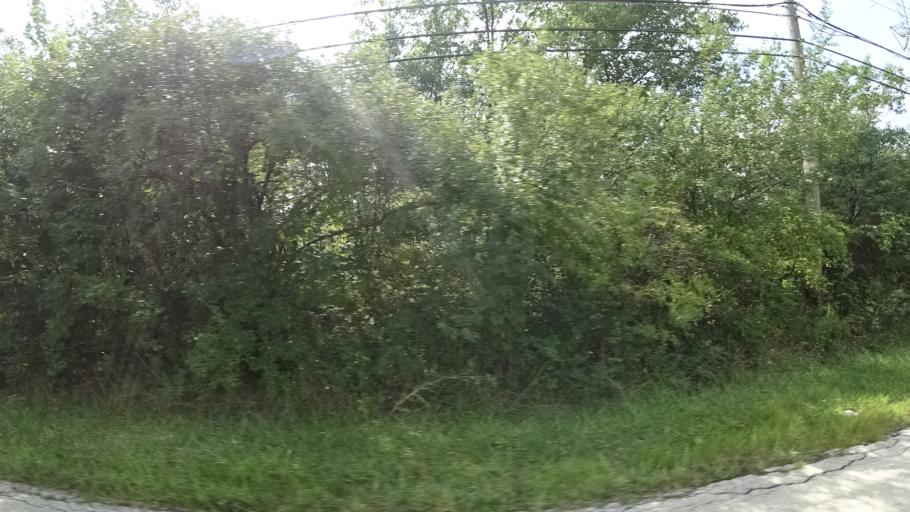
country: US
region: Illinois
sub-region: Will County
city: Goodings Grove
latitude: 41.6531
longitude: -87.8929
